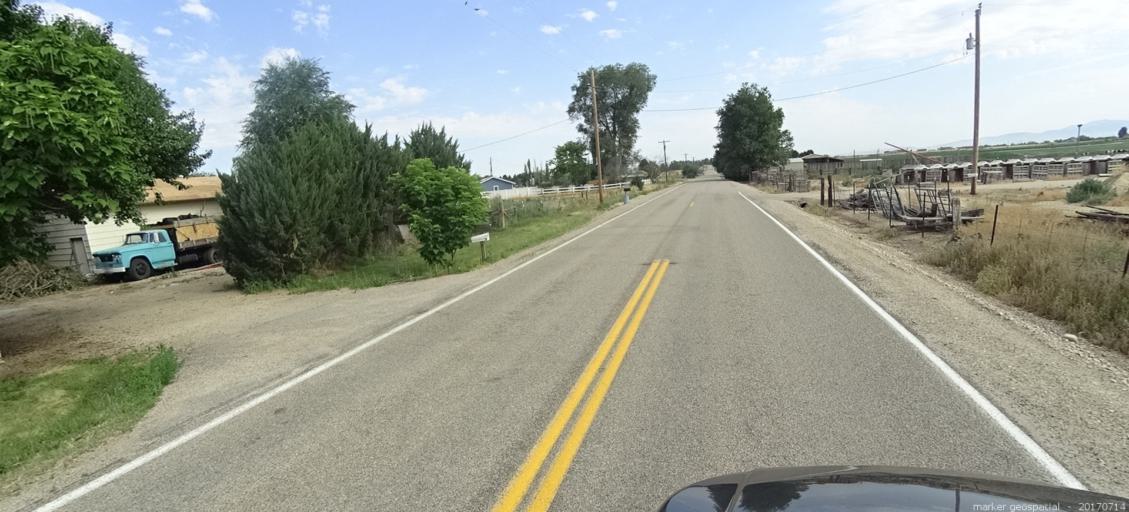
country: US
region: Idaho
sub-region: Ada County
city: Kuna
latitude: 43.4747
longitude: -116.3545
